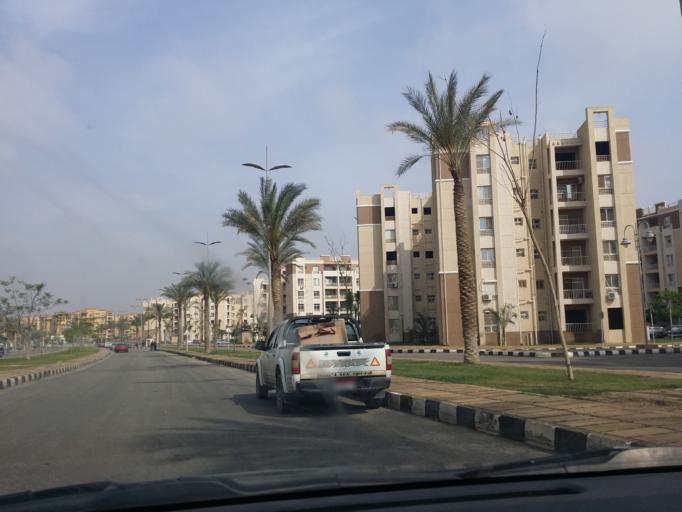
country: EG
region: Muhafazat al Qalyubiyah
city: Al Khankah
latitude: 30.0839
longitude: 31.6472
